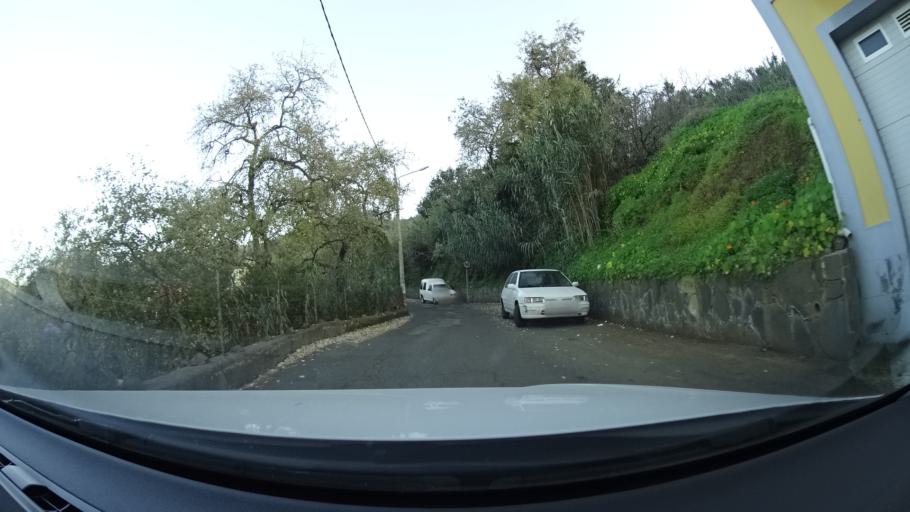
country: ES
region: Canary Islands
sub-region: Provincia de Las Palmas
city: Teror
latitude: 28.0579
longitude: -15.5442
